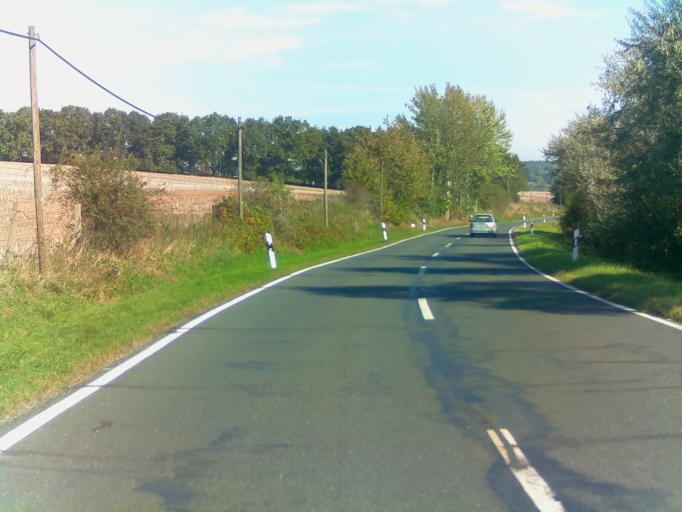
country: DE
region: Thuringia
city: Saara
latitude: 50.8469
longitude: 11.9675
